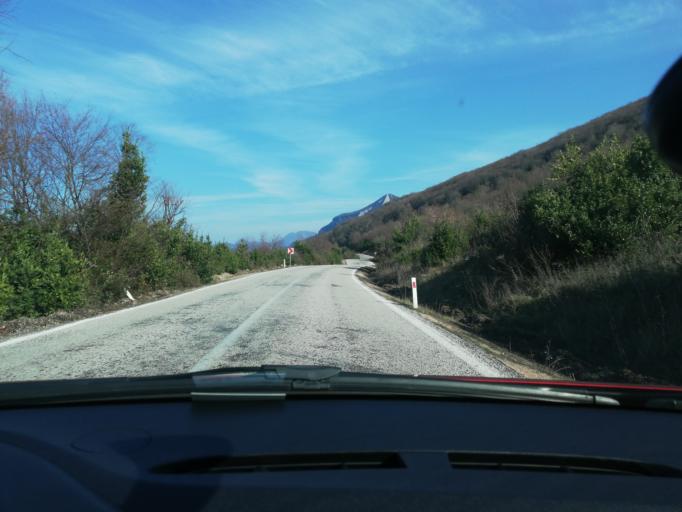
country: TR
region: Bartin
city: Kurucasile
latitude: 41.8585
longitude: 32.7834
